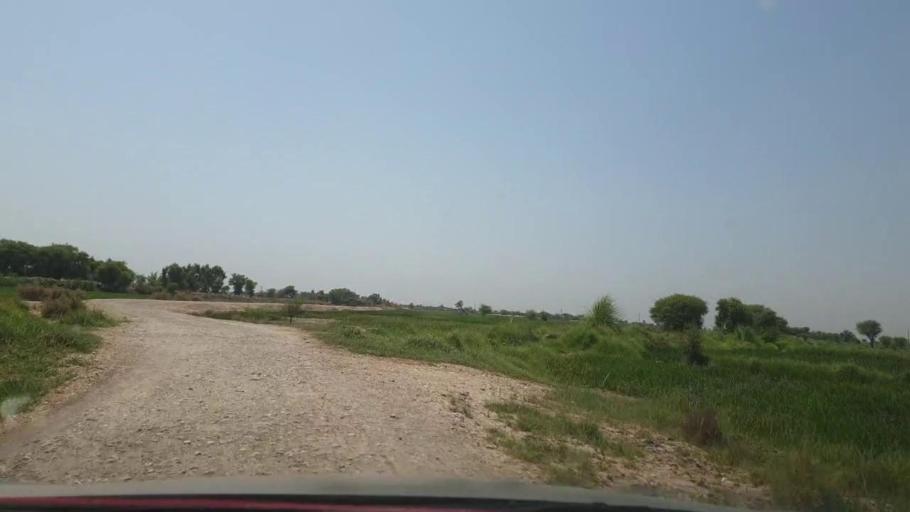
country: PK
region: Sindh
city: Warah
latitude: 27.4874
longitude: 67.7372
